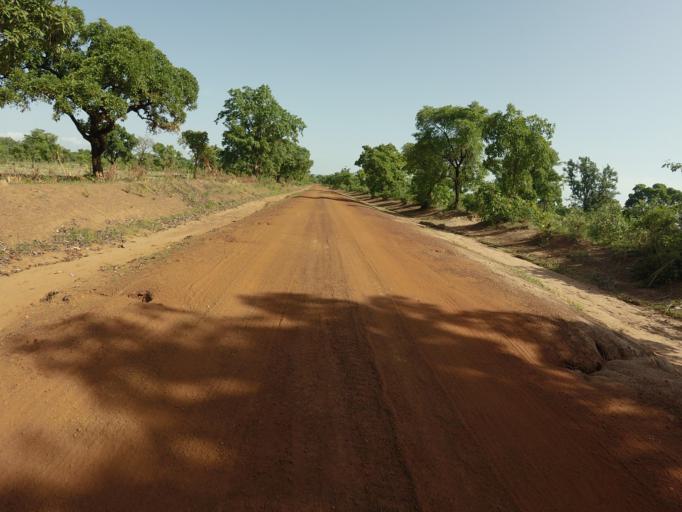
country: GH
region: Upper East
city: Bawku
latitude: 10.7448
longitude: -0.2004
